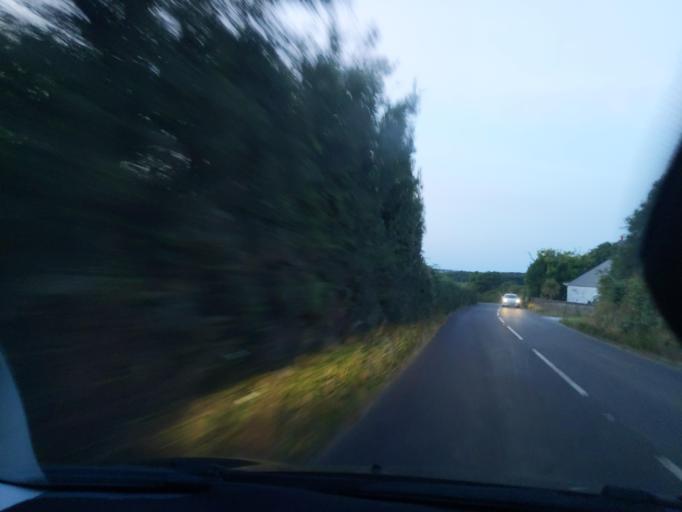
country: GB
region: England
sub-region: Cornwall
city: Camborne
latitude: 50.1877
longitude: -5.3087
